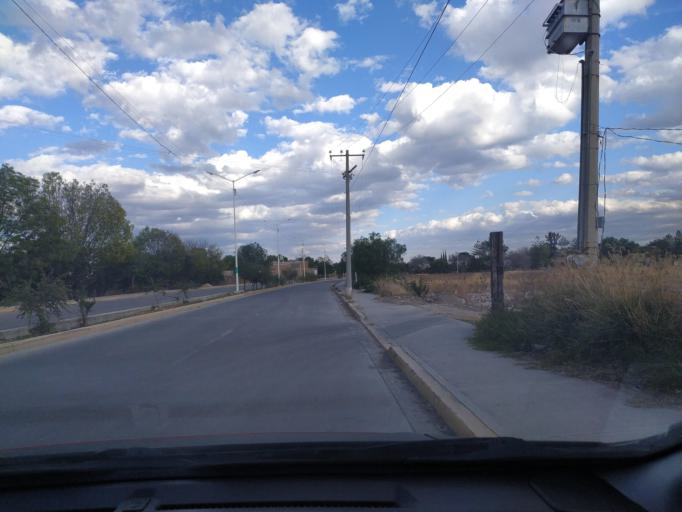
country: LA
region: Oudomxai
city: Muang La
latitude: 21.0178
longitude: 101.8360
